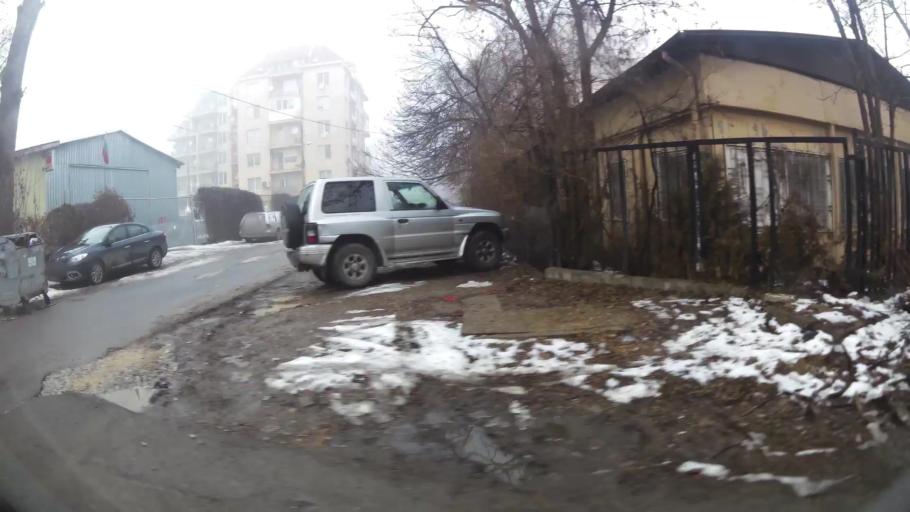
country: BG
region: Sofia-Capital
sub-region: Stolichna Obshtina
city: Sofia
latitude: 42.6633
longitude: 23.2576
